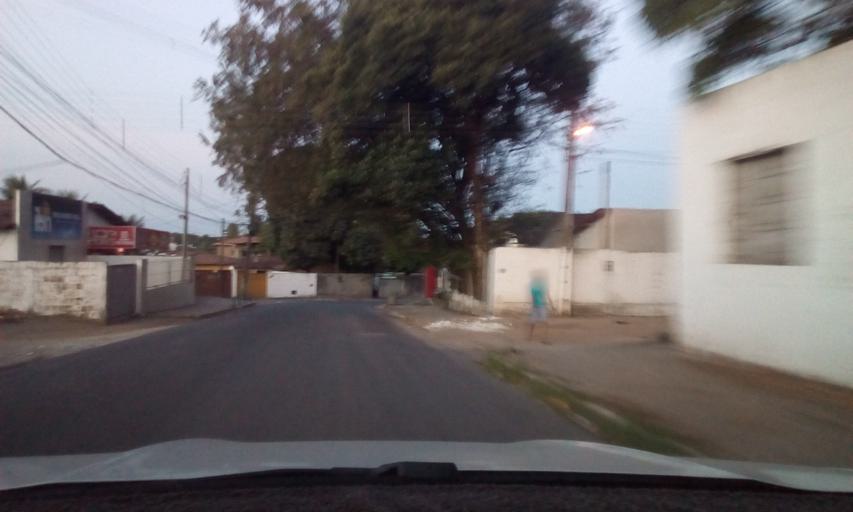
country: BR
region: Paraiba
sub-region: Bayeux
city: Bayeux
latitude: -7.1685
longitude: -34.9103
